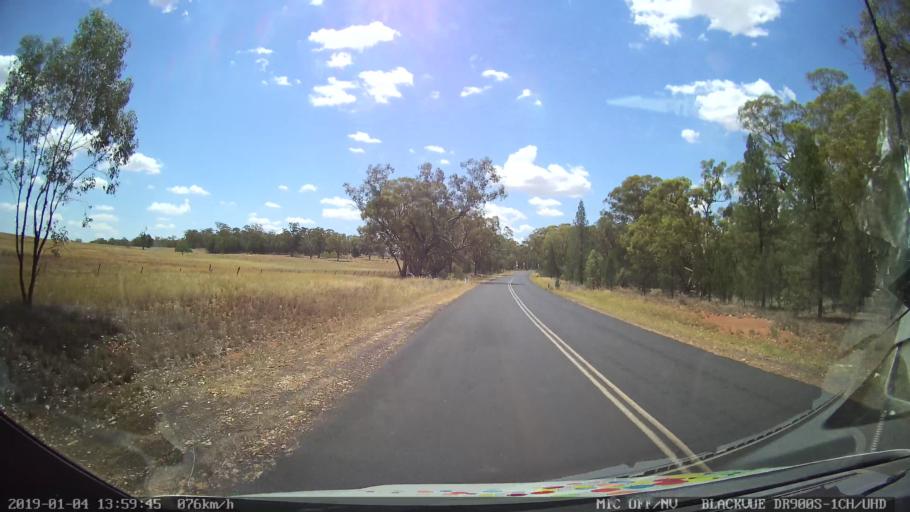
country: AU
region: New South Wales
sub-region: Dubbo Municipality
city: Dubbo
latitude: -32.3135
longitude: 148.5887
